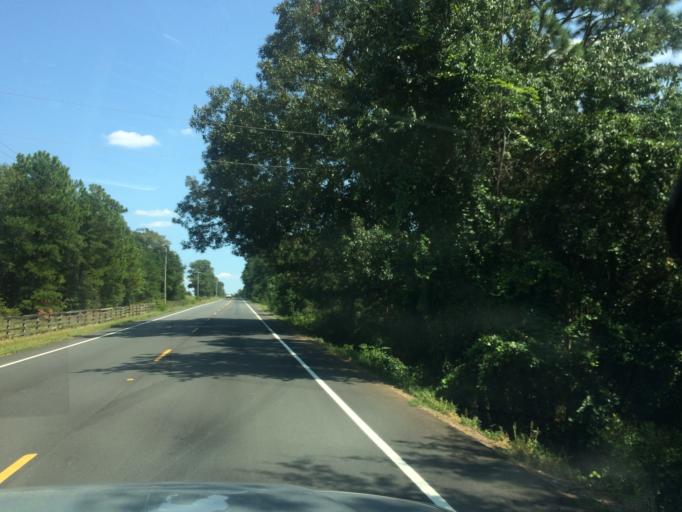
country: US
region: South Carolina
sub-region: Aiken County
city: Aiken
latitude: 33.5722
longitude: -81.5336
